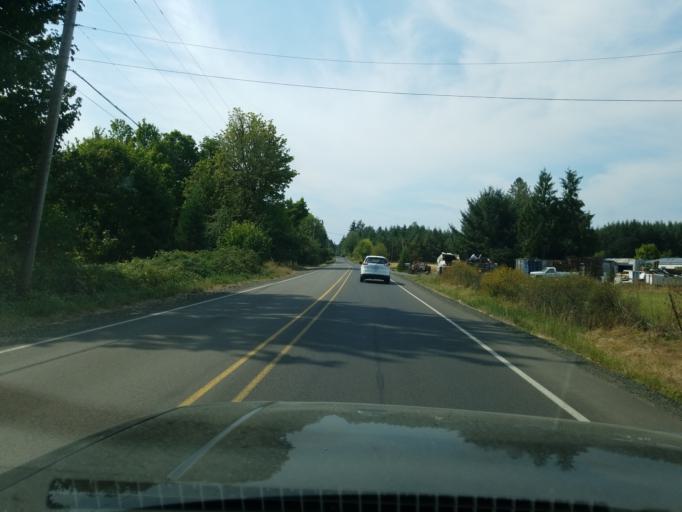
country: US
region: Oregon
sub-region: Polk County
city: Grand Ronde
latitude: 45.0801
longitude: -123.6187
